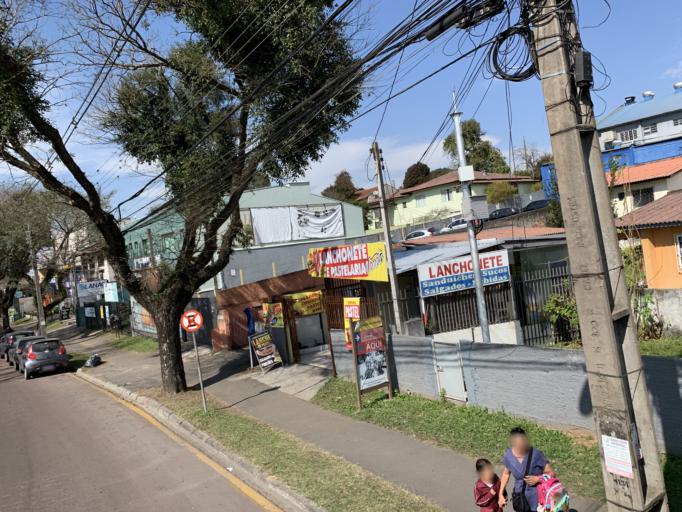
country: BR
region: Parana
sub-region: Curitiba
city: Curitiba
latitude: -25.4018
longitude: -49.3295
